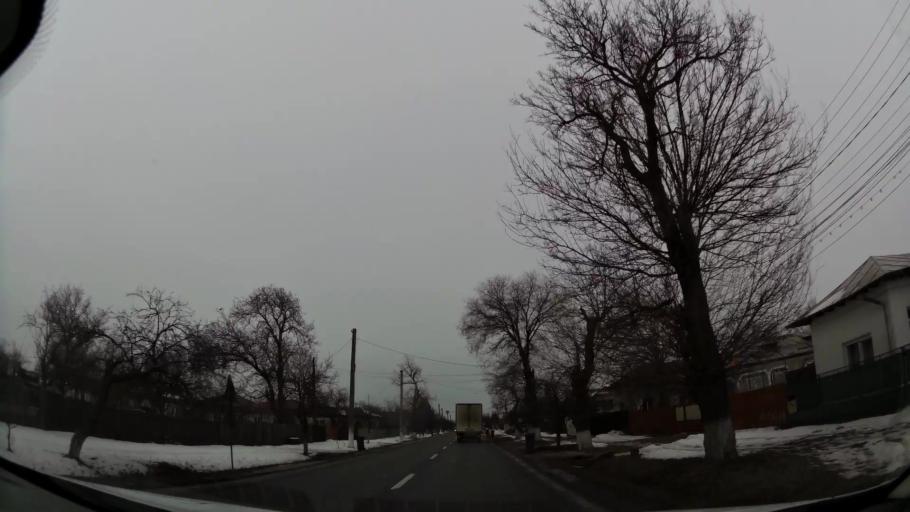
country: RO
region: Dambovita
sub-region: Comuna Tartasesti
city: Baldana
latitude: 44.6000
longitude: 25.7820
